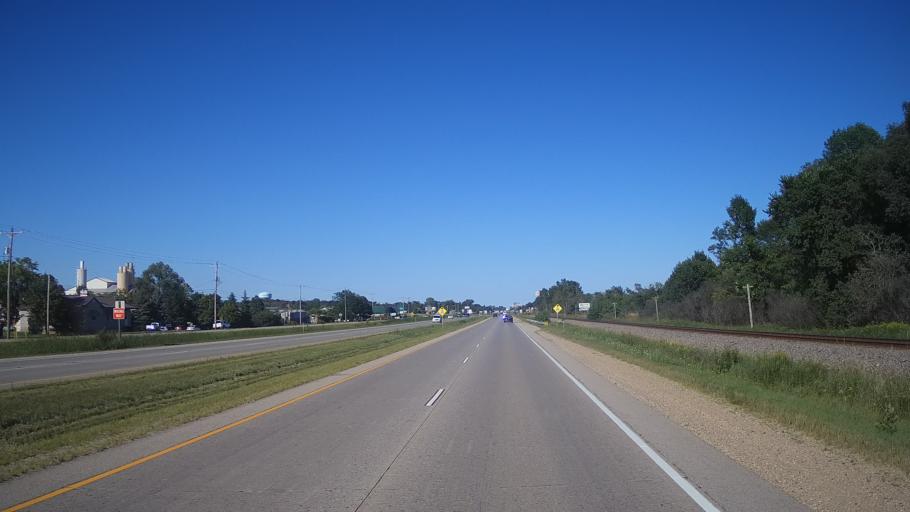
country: US
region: Wisconsin
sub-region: Marinette County
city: Marinette
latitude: 45.0737
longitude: -87.6763
